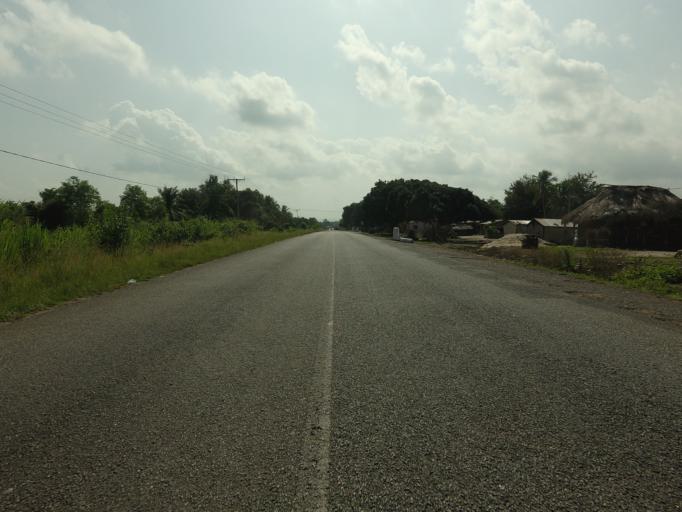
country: GH
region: Volta
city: Ho
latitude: 6.5738
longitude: 0.5938
